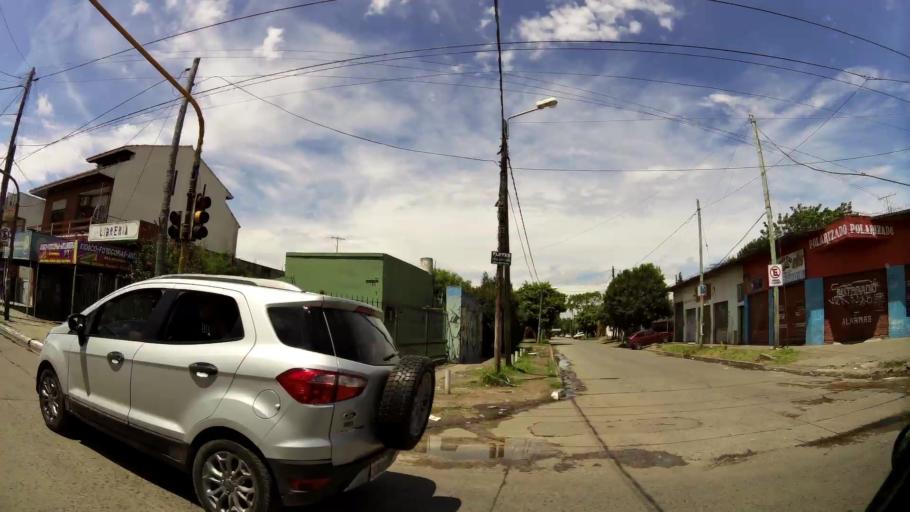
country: AR
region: Buenos Aires
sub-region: Partido de Quilmes
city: Quilmes
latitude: -34.7889
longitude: -58.2775
